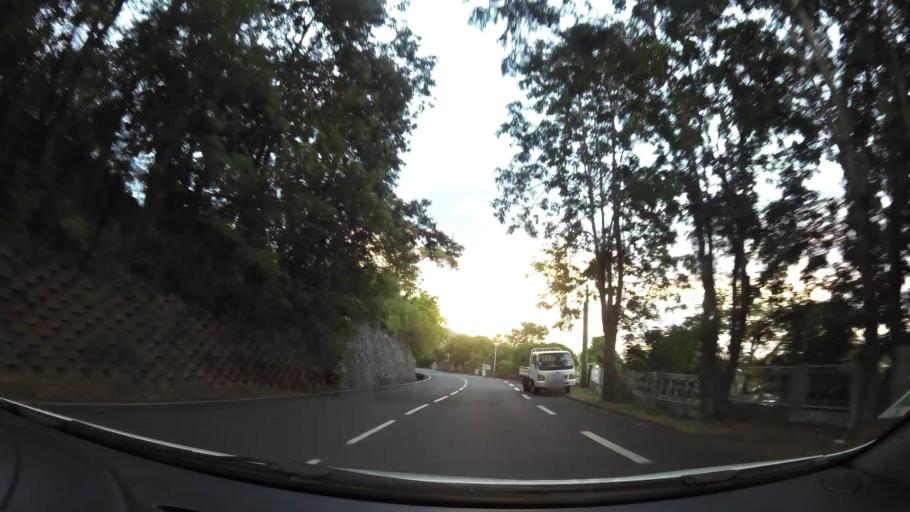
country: RE
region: Reunion
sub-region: Reunion
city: Saint-Denis
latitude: -20.9042
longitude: 55.4642
